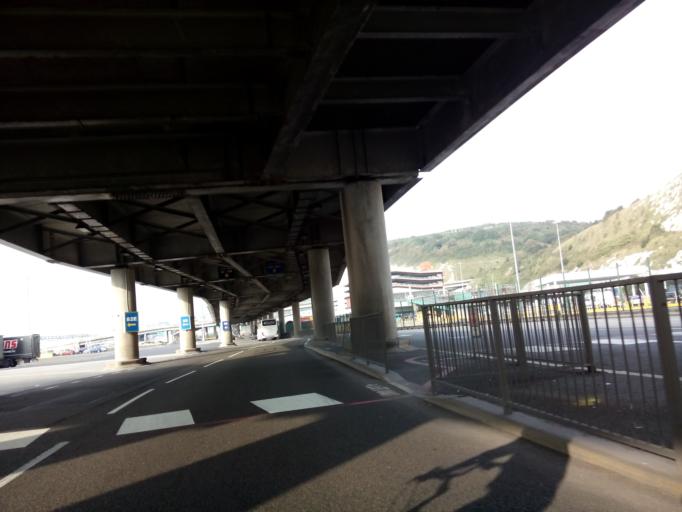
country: GB
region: England
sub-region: Kent
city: Dover
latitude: 51.1286
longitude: 1.3361
